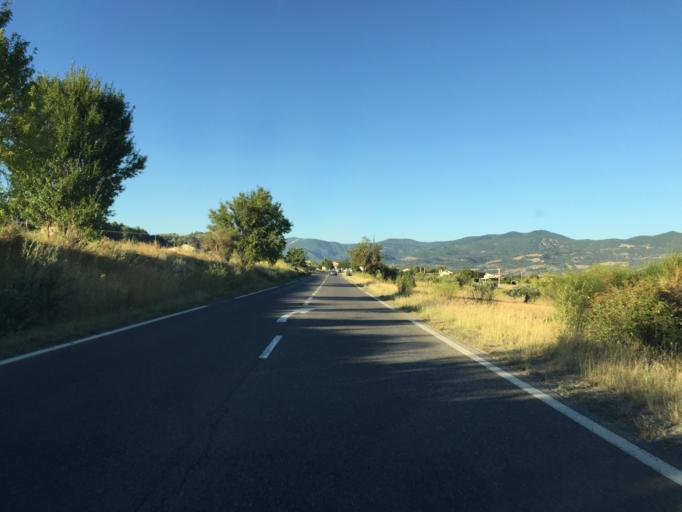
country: FR
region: Provence-Alpes-Cote d'Azur
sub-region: Departement des Alpes-de-Haute-Provence
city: Les Mees
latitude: 44.0599
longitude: 5.9738
